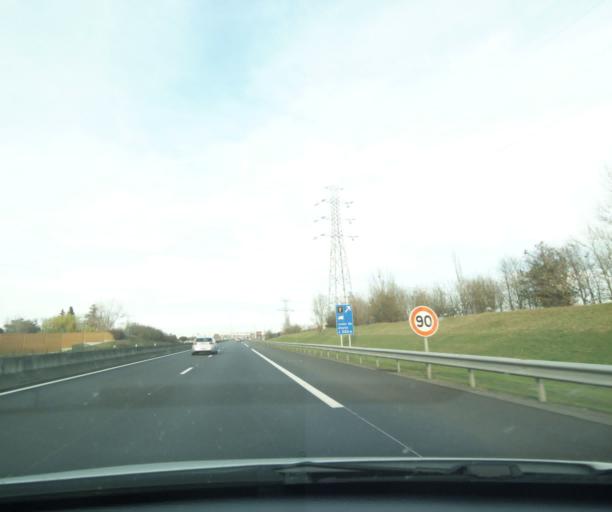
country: FR
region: Midi-Pyrenees
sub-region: Departement de la Haute-Garonne
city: Villeneuve-Tolosane
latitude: 43.5025
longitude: 1.3464
